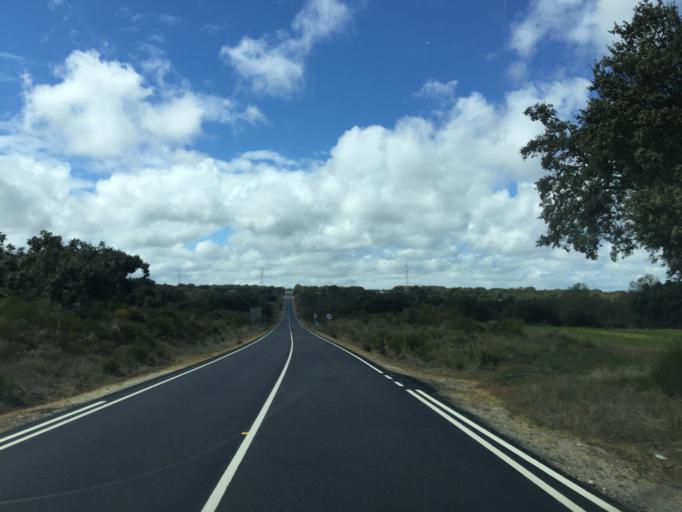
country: ES
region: Castille and Leon
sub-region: Provincia de Zamora
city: Moralina
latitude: 41.4827
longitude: -6.1243
